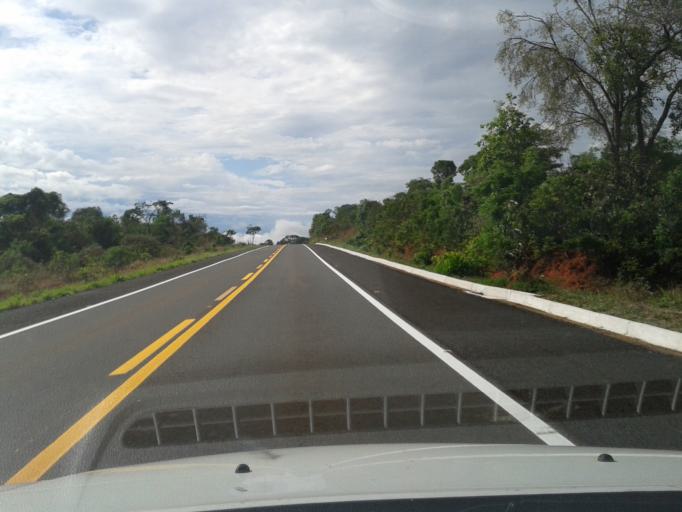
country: BR
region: Minas Gerais
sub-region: Campina Verde
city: Campina Verde
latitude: -19.3193
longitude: -49.6600
